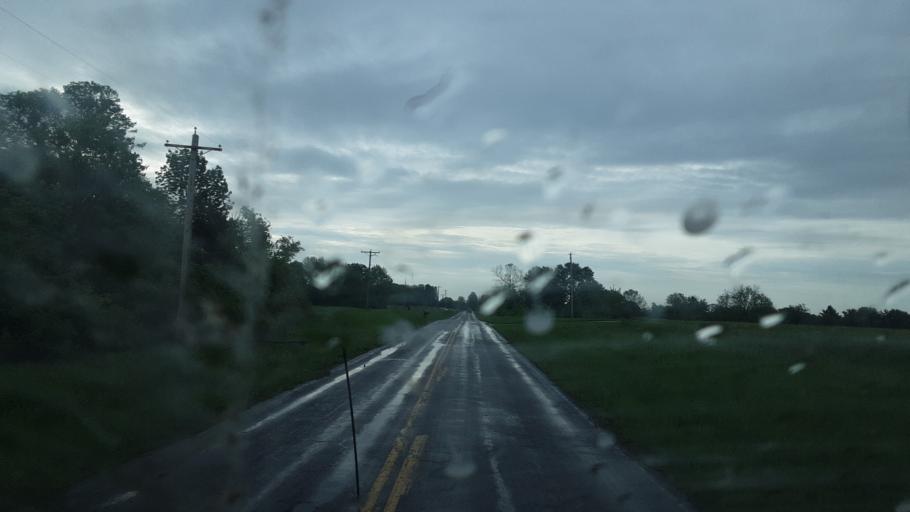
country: US
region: Missouri
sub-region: Clark County
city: Kahoka
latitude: 40.4371
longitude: -91.5948
